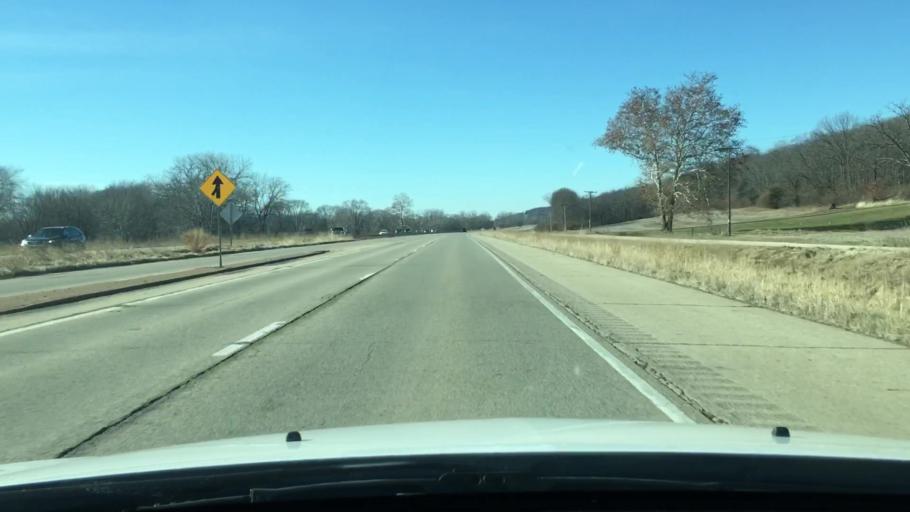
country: US
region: Illinois
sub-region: Peoria County
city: Glasford
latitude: 40.5613
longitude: -89.7522
